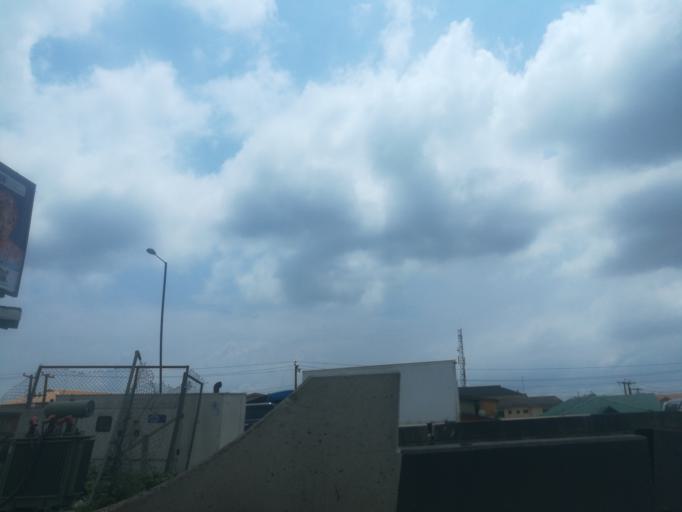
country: NG
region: Lagos
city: Ojota
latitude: 6.5709
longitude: 3.3971
